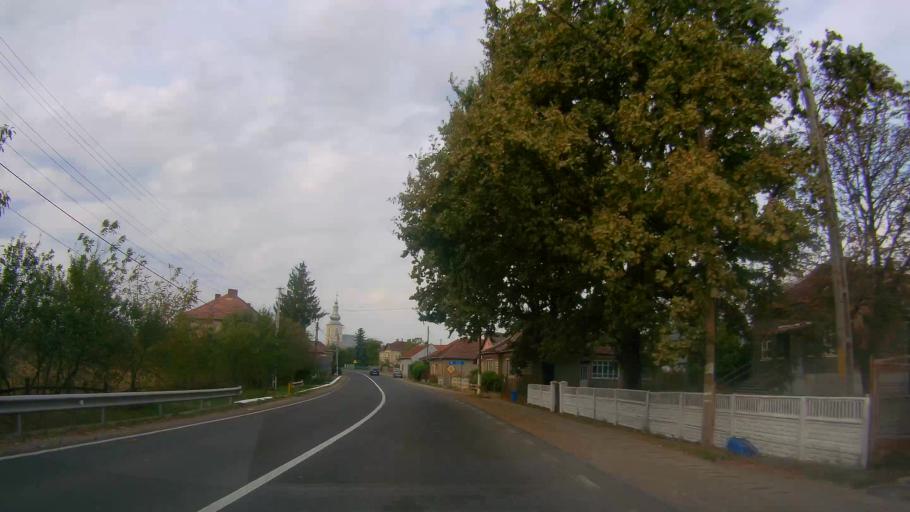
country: RO
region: Satu Mare
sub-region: Comuna Beltiug
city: Beltiug
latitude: 47.5841
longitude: 22.8833
